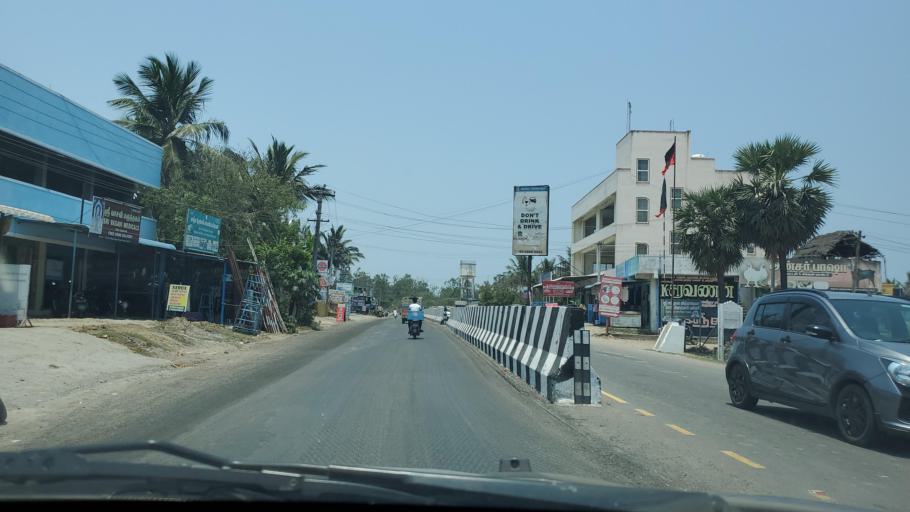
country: IN
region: Tamil Nadu
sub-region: Kancheepuram
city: Vengavasal
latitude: 12.8653
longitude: 80.1757
